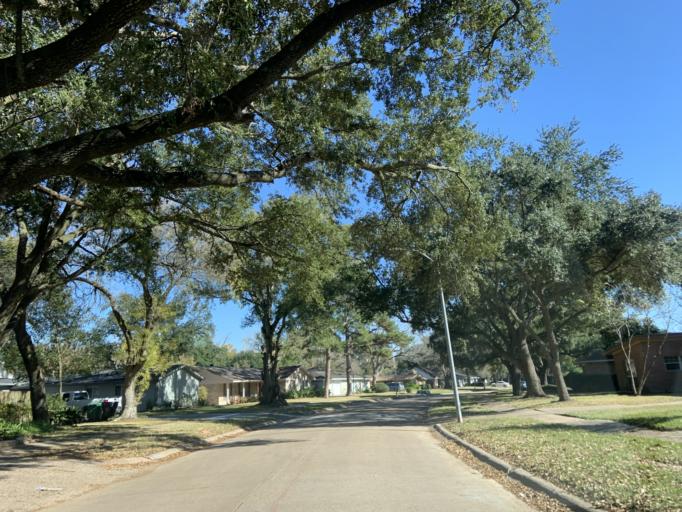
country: US
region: Texas
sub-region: Harris County
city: Bellaire
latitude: 29.6802
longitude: -95.5011
